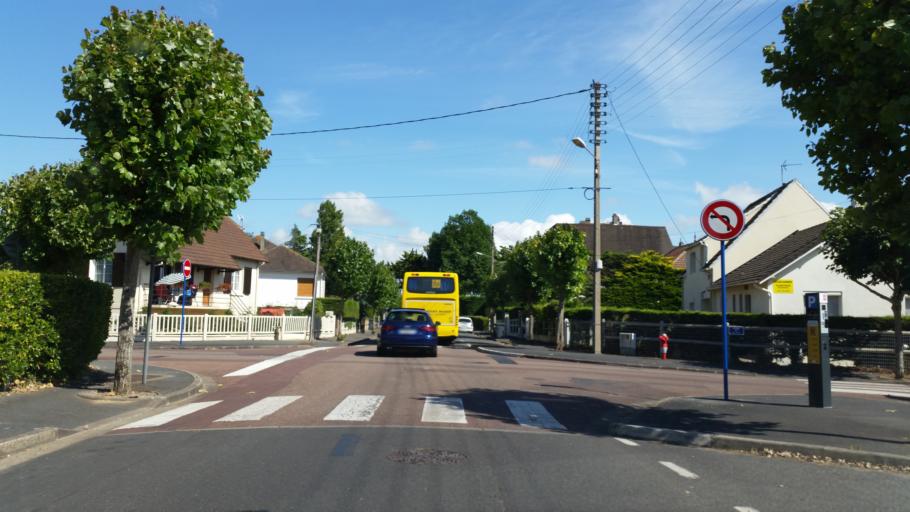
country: FR
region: Lower Normandy
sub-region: Departement du Calvados
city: Ouistreham
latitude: 49.2870
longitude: -0.2514
